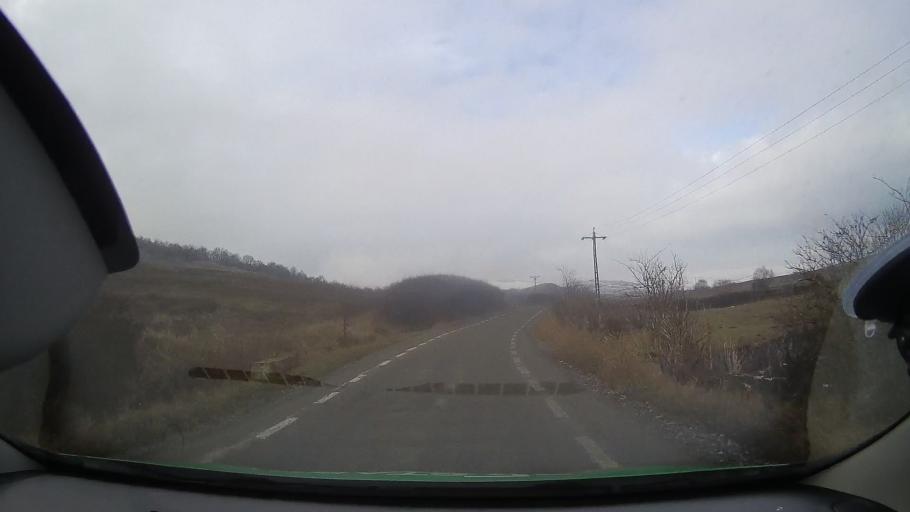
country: RO
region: Mures
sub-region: Comuna Atintis
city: Atintis
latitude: 46.4080
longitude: 24.0857
